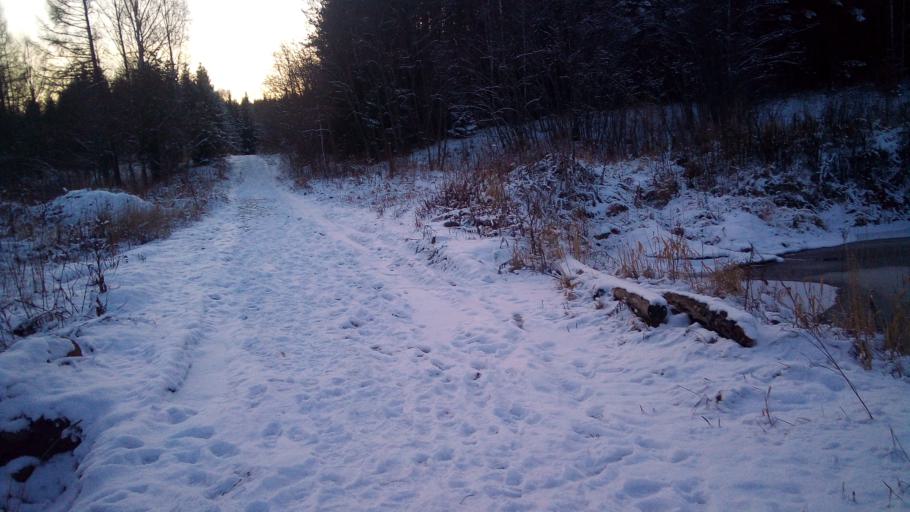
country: RU
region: Chelyabinsk
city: Bakal
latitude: 54.8145
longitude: 59.0004
